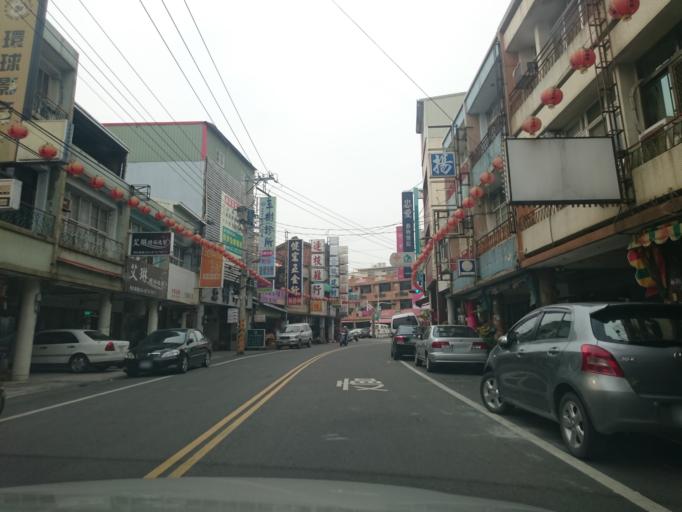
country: TW
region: Taiwan
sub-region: Nantou
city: Nantou
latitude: 23.8622
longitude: 120.5850
